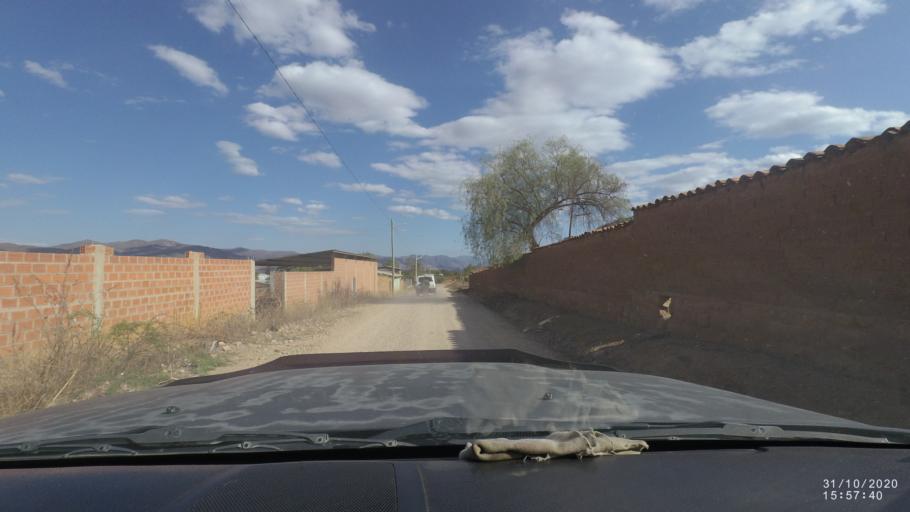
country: BO
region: Chuquisaca
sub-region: Provincia Zudanez
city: Mojocoya
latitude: -18.3247
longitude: -64.6747
